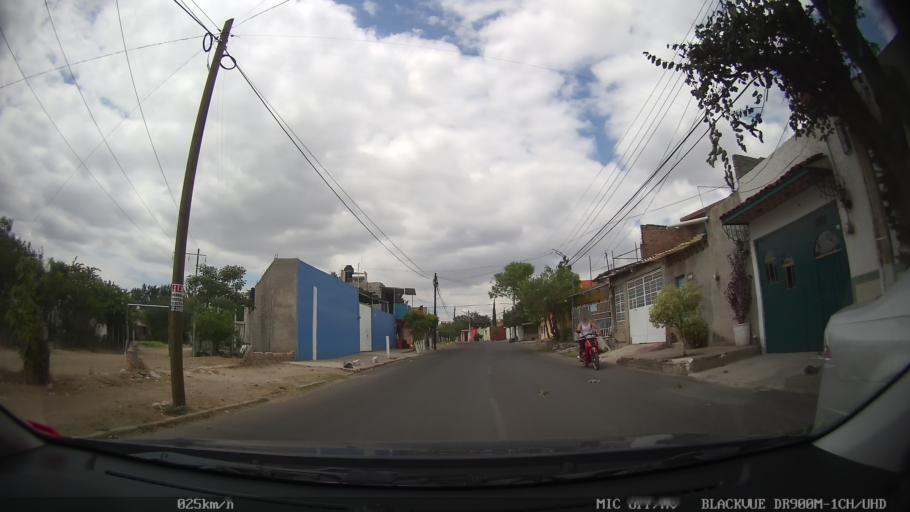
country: MX
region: Jalisco
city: Tlaquepaque
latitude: 20.6389
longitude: -103.2634
